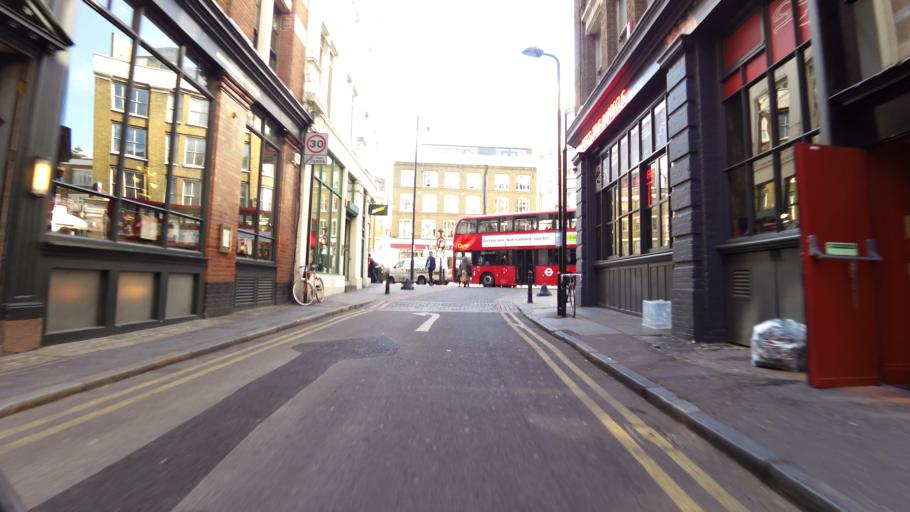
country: GB
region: England
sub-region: Greater London
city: Barbican
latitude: 51.5252
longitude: -0.0811
